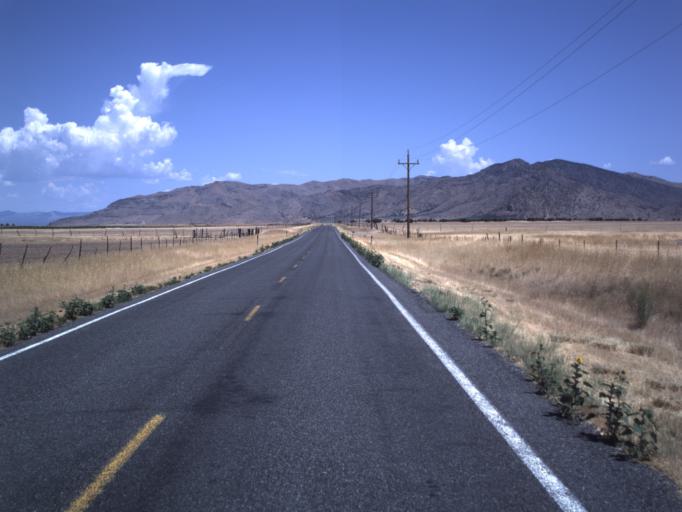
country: US
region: Utah
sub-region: Millard County
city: Delta
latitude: 39.5007
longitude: -112.2690
